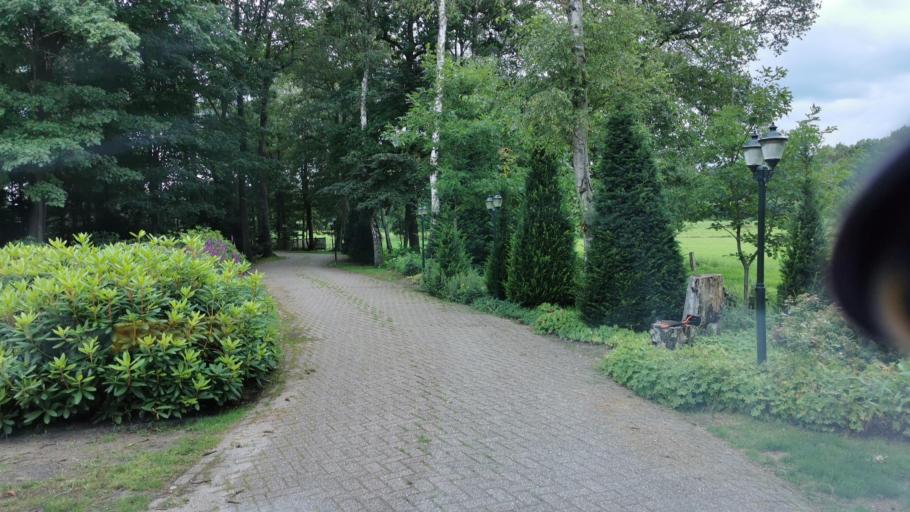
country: NL
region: Overijssel
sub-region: Gemeente Enschede
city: Enschede
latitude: 52.2465
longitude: 6.9356
